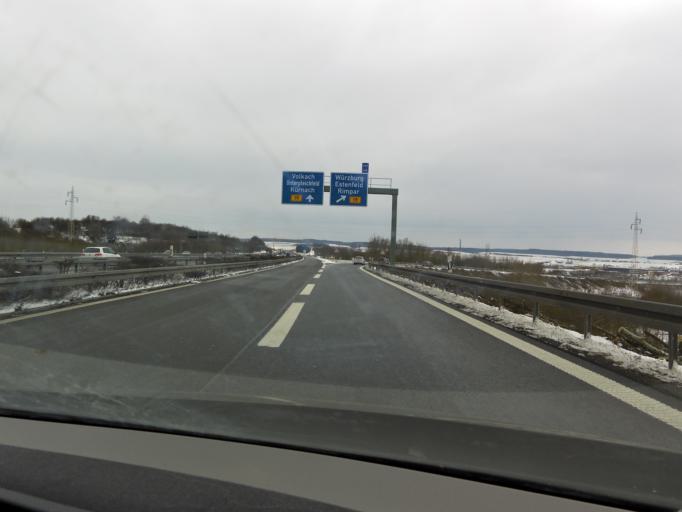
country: DE
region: Bavaria
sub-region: Regierungsbezirk Unterfranken
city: Estenfeld
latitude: 49.8483
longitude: 10.0063
